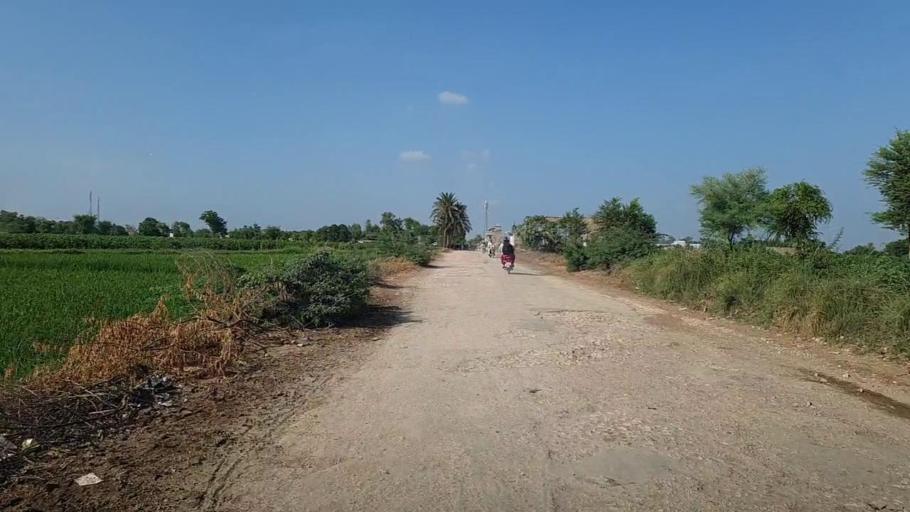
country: PK
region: Sindh
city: Kandiaro
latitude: 27.0773
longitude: 68.3135
